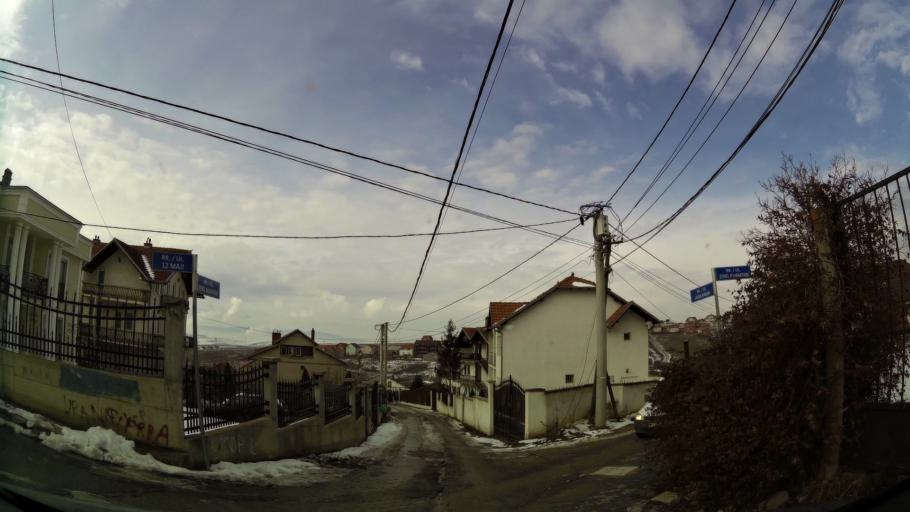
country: XK
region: Pristina
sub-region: Komuna e Prishtines
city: Pristina
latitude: 42.6789
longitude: 21.1571
